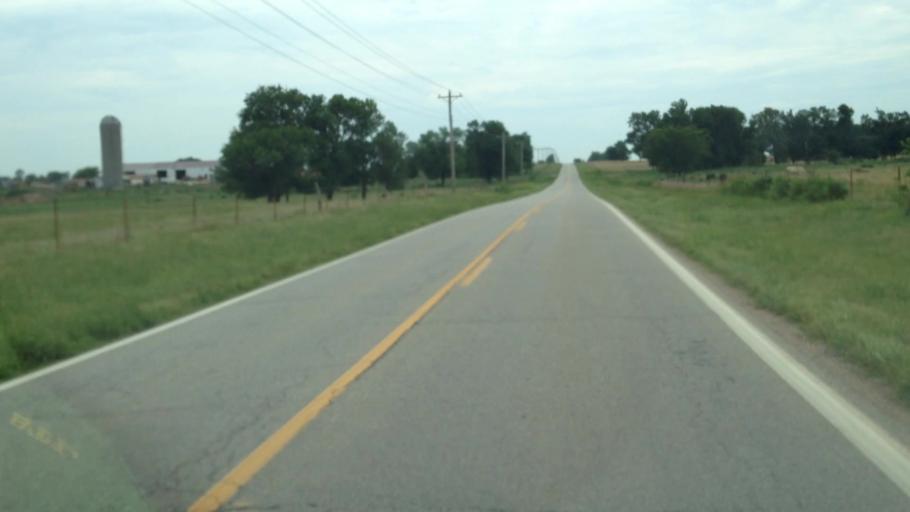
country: US
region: Oklahoma
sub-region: Delaware County
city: Cleora
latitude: 36.6022
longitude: -94.9634
